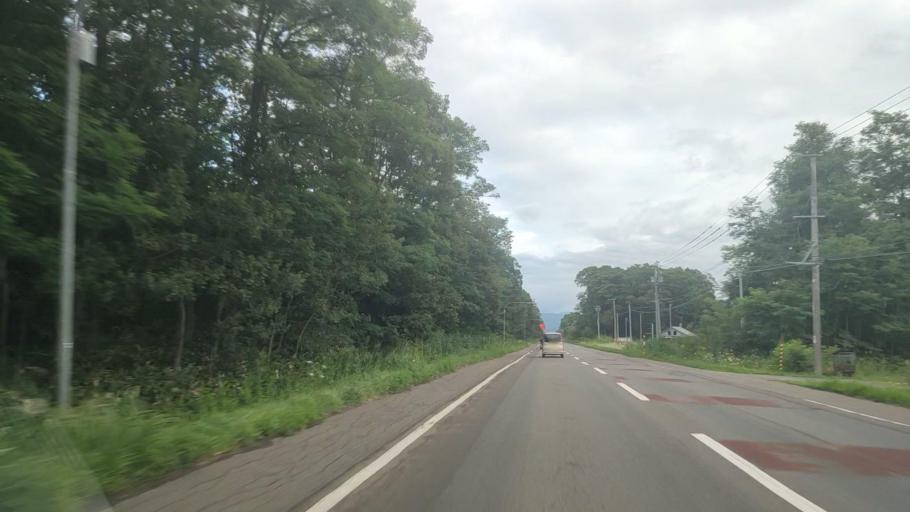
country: JP
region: Hokkaido
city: Nanae
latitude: 42.0191
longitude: 140.6190
